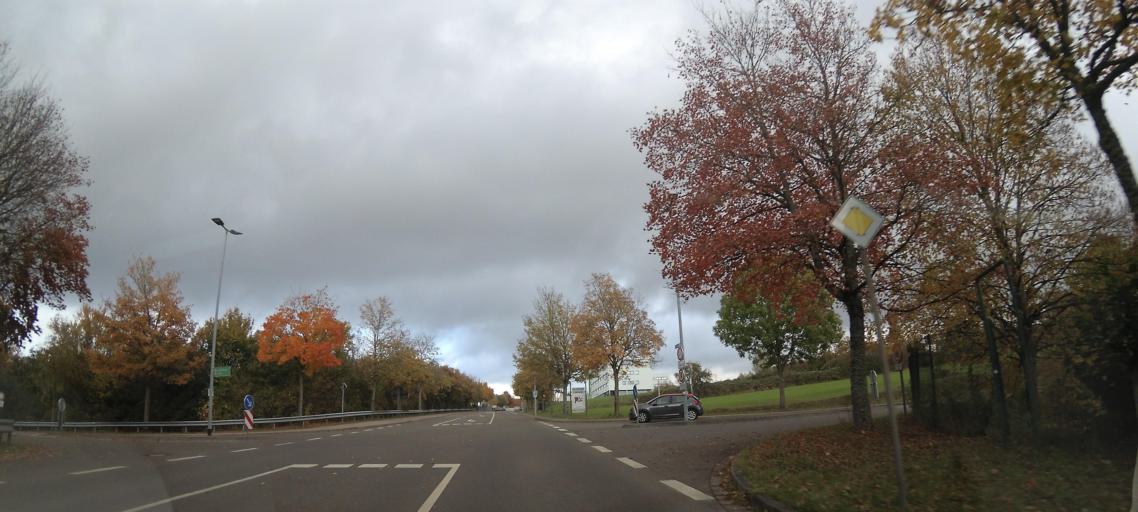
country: DE
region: Rheinland-Pfalz
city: Vinningen
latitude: 49.1823
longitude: 7.5649
